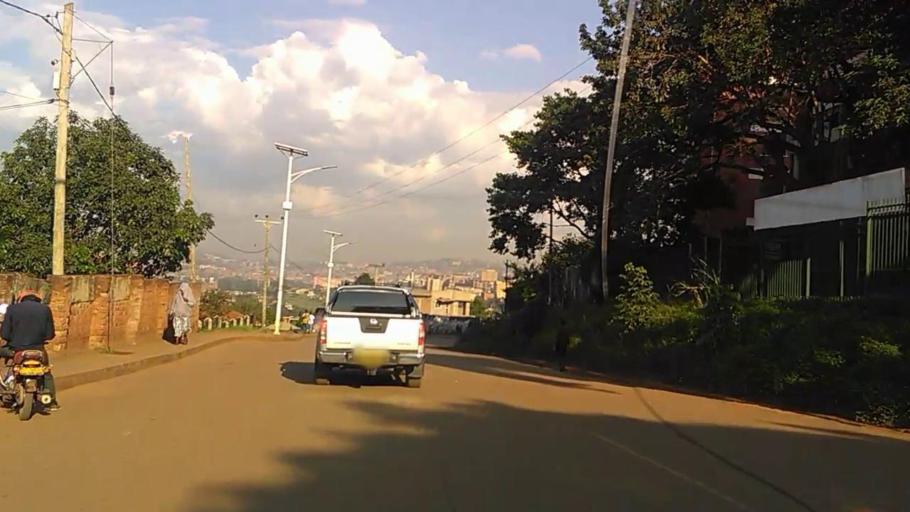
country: UG
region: Central Region
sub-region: Kampala District
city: Kampala
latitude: 0.3085
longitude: 32.5956
